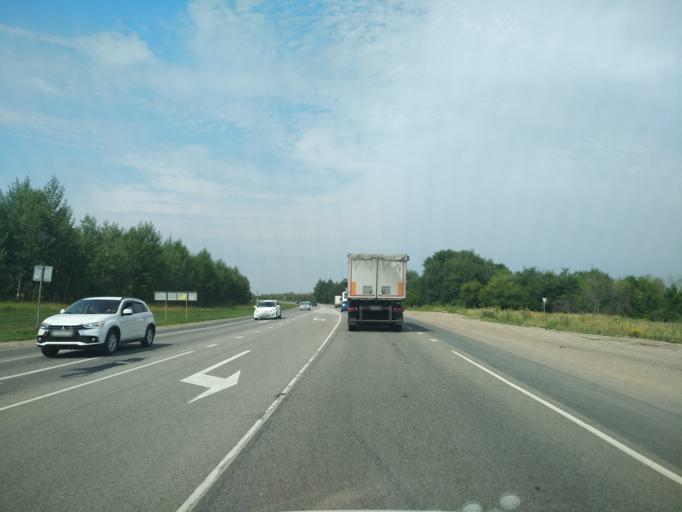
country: RU
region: Voronezj
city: Novaya Usman'
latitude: 51.7011
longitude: 39.4213
